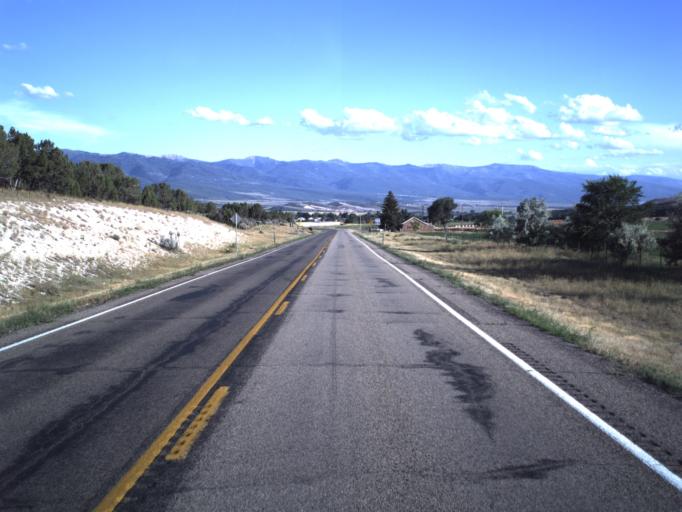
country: US
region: Utah
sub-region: Sanpete County
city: Fairview
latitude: 39.6467
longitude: -111.4506
